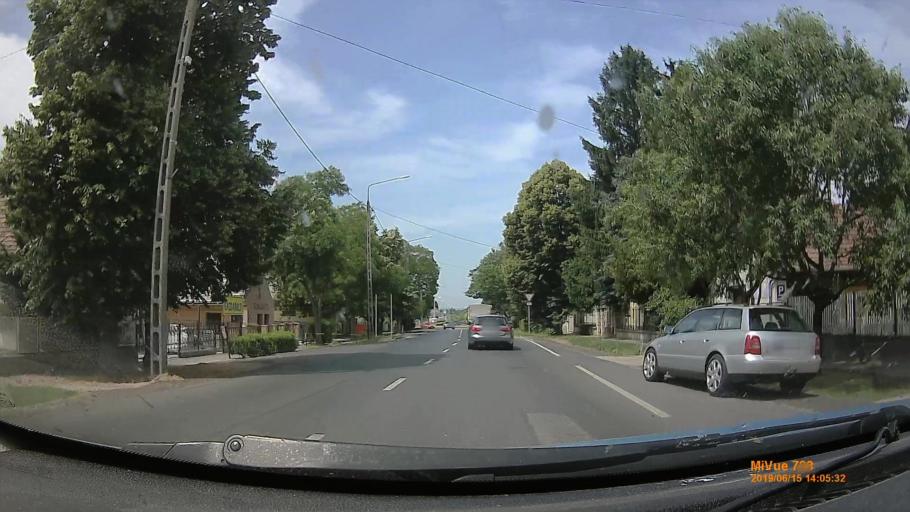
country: HU
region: Somogy
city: Siofok
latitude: 46.8838
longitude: 18.0678
